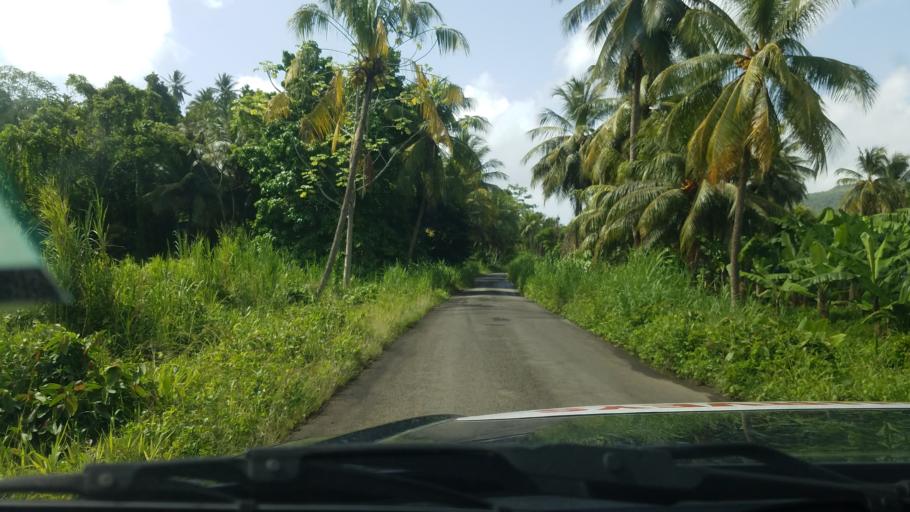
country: LC
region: Anse-la-Raye
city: Anse La Raye
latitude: 13.9539
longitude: -61.0023
